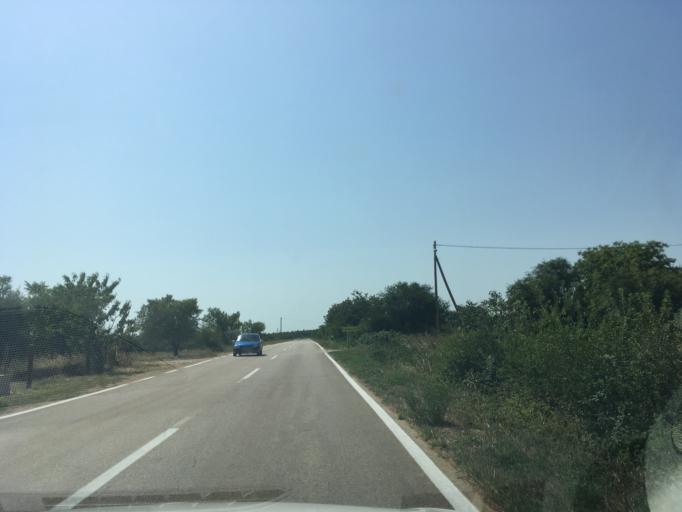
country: HR
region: Zadarska
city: Benkovac
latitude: 43.9644
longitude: 15.7466
